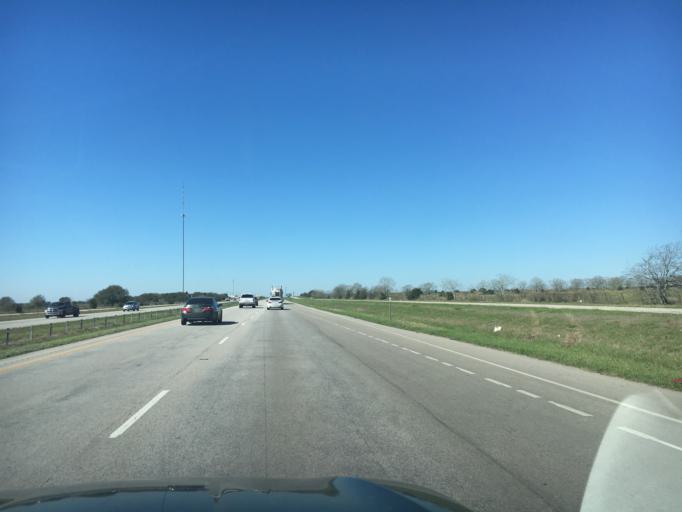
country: US
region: Texas
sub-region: Colorado County
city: Eagle Lake
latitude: 29.7405
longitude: -96.3360
